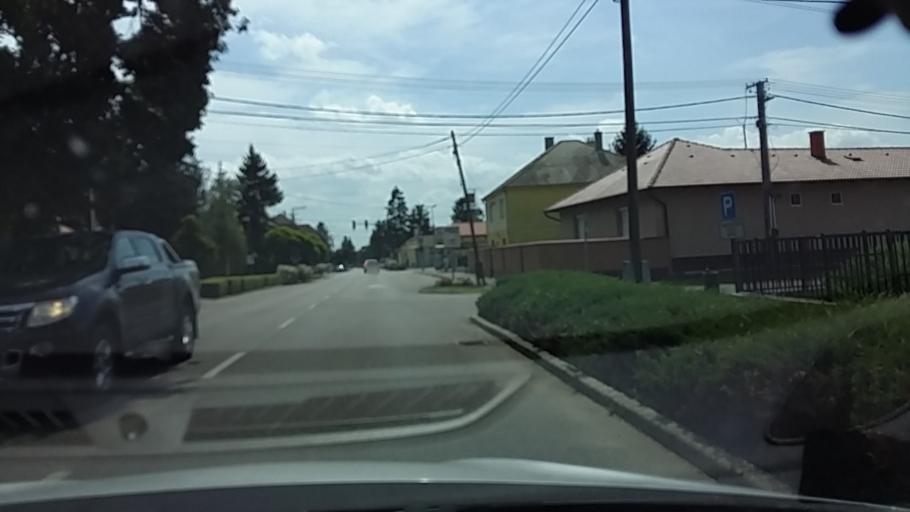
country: HU
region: Borsod-Abauj-Zemplen
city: Nyekladhaza
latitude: 47.9934
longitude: 20.8359
